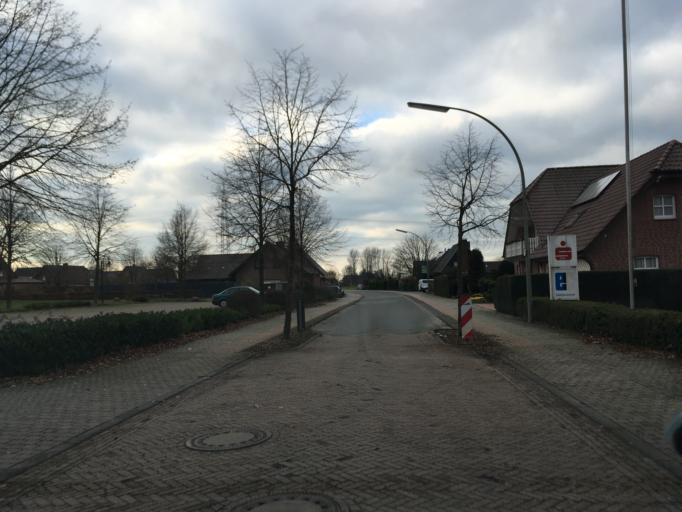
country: DE
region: North Rhine-Westphalia
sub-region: Regierungsbezirk Munster
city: Ahaus
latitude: 52.1242
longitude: 6.9870
